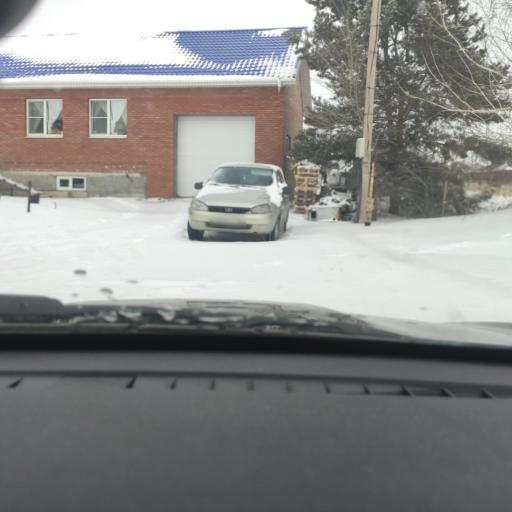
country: RU
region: Samara
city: Tol'yatti
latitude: 53.5538
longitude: 49.3809
